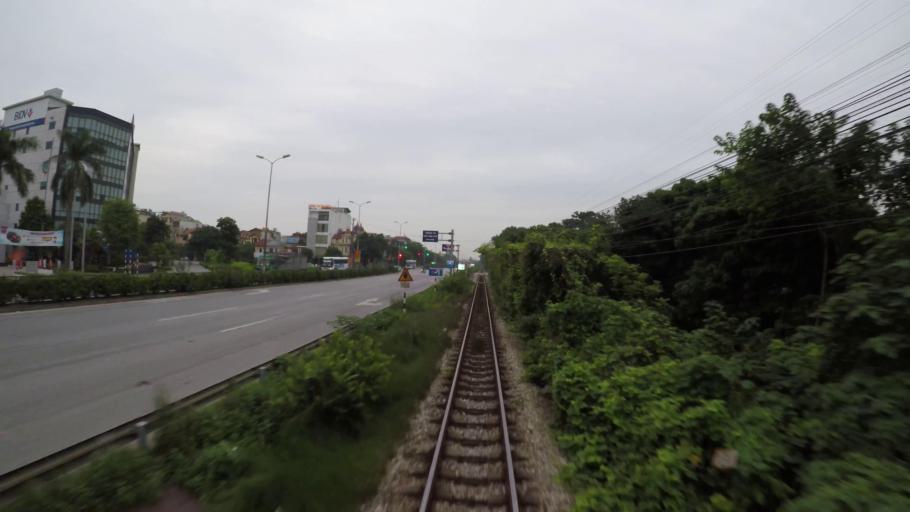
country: VN
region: Ha Noi
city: Trau Quy
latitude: 21.0043
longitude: 105.9613
